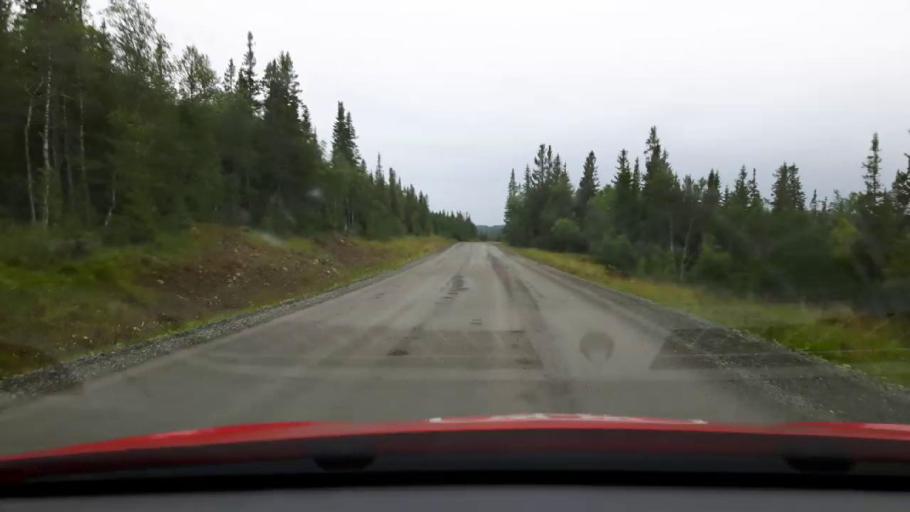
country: NO
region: Nord-Trondelag
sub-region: Meraker
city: Meraker
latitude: 63.5421
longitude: 12.3802
